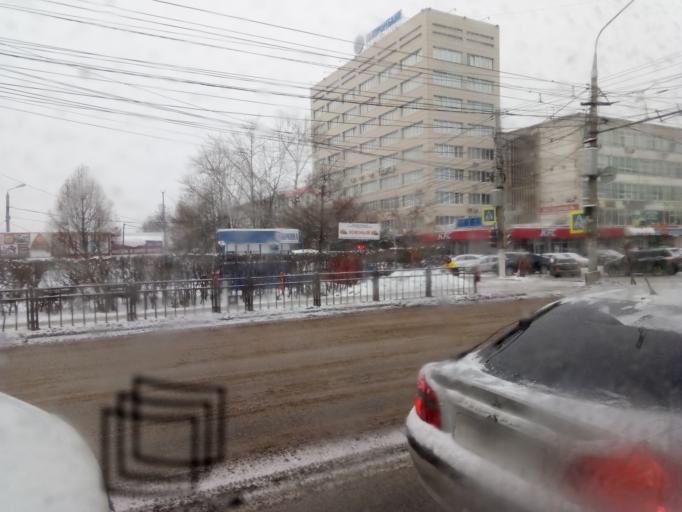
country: RU
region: Tula
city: Mendeleyevskiy
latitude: 54.1580
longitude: 37.5852
